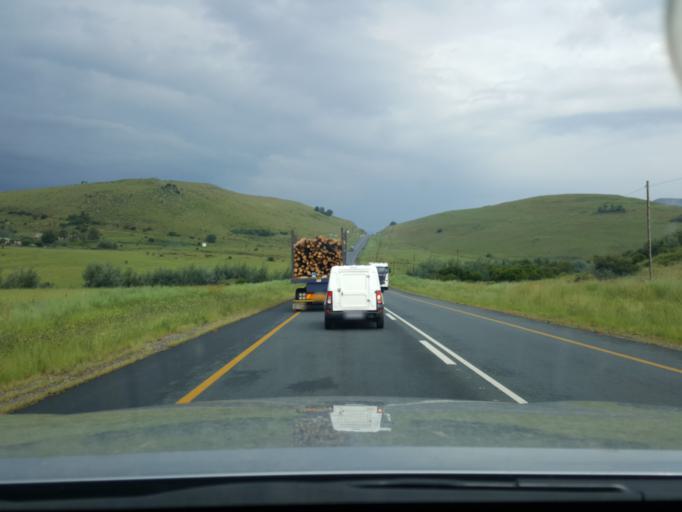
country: ZA
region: Mpumalanga
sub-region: Nkangala District Municipality
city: Belfast
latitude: -25.6223
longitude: 30.3040
